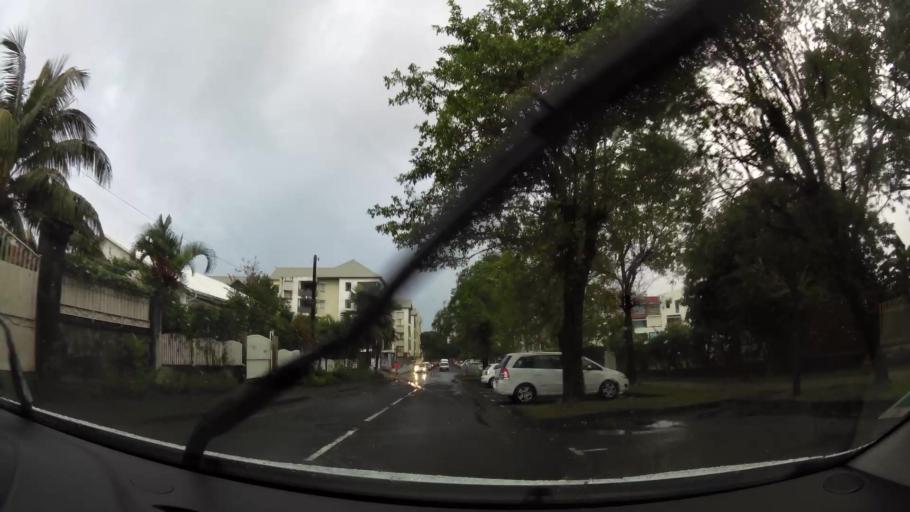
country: RE
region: Reunion
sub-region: Reunion
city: Saint-Benoit
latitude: -21.0369
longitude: 55.7120
